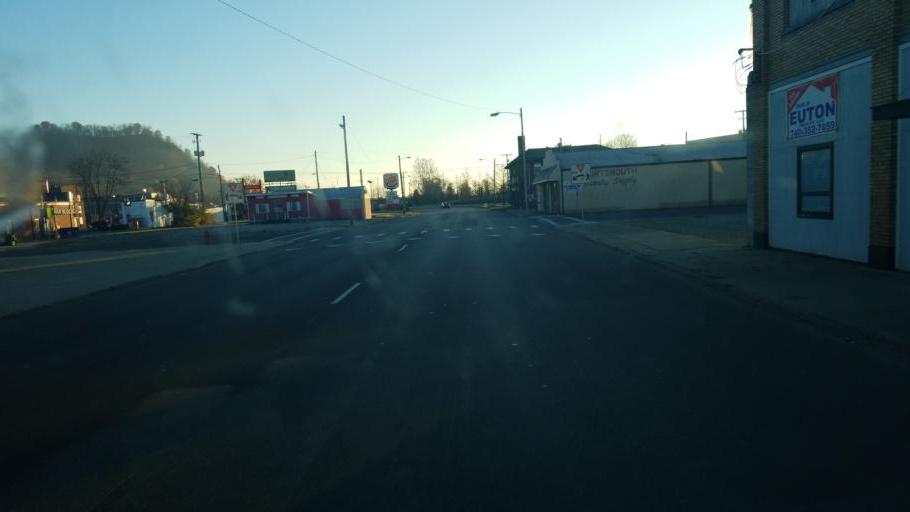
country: US
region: Kentucky
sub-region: Greenup County
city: South Shore
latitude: 38.7386
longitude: -82.9743
